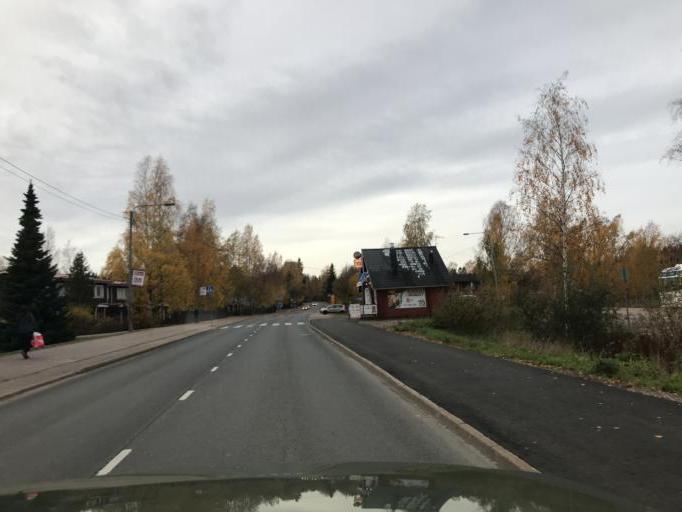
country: FI
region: Uusimaa
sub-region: Helsinki
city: Vantaa
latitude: 60.2505
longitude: 25.0915
